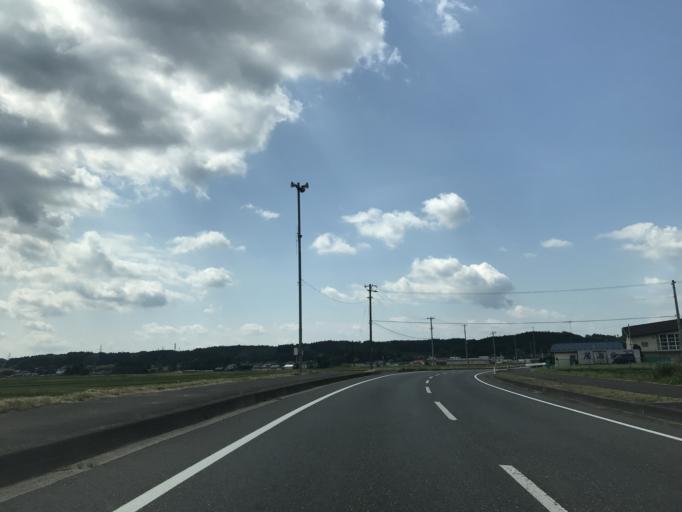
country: JP
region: Miyagi
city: Furukawa
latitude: 38.7400
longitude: 140.9600
